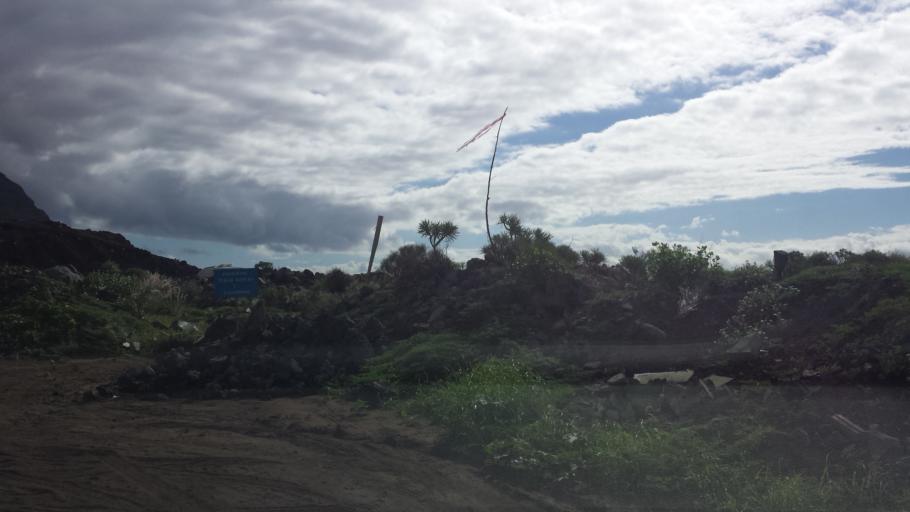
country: ES
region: Canary Islands
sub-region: Provincia de Santa Cruz de Tenerife
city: Fuencaliente de la Palma
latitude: 28.5522
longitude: -17.8860
